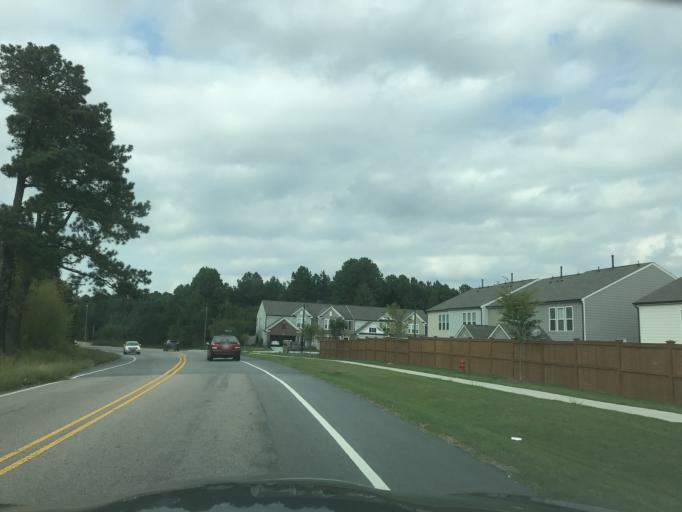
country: US
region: North Carolina
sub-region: Durham County
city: Durham
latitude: 35.9067
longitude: -78.9164
